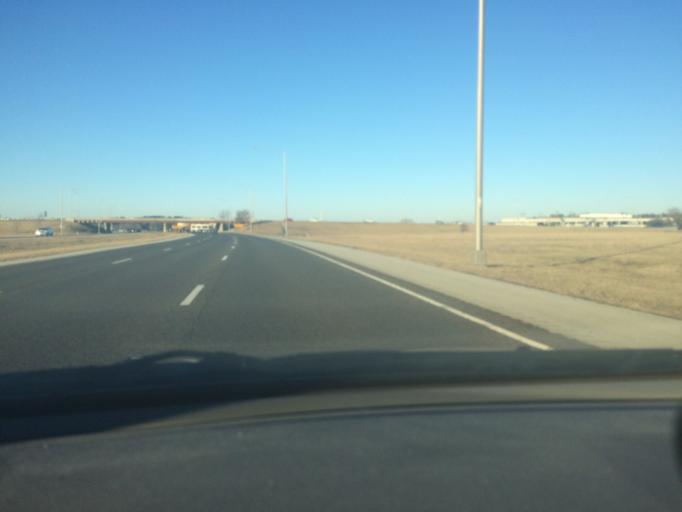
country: US
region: Illinois
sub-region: Cook County
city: Palatine
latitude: 42.1364
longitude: -88.0046
